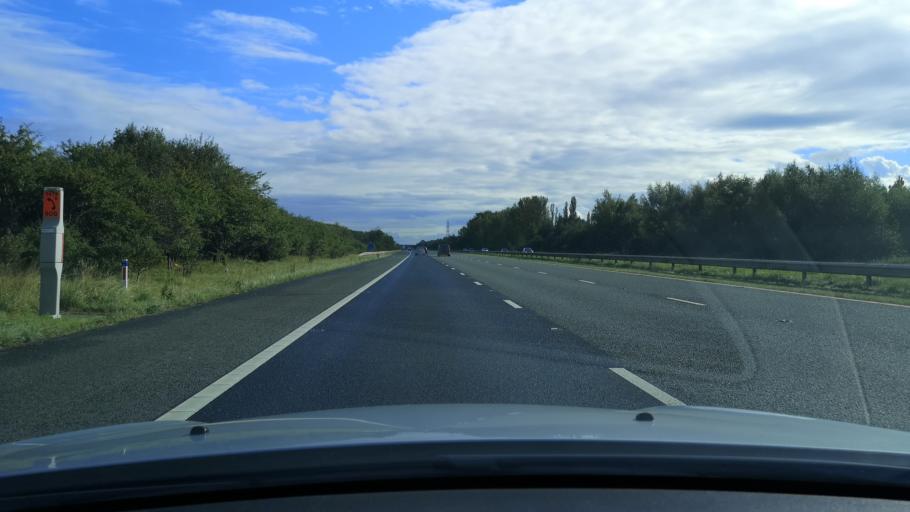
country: GB
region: England
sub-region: East Riding of Yorkshire
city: Pollington
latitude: 53.6829
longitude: -1.0718
